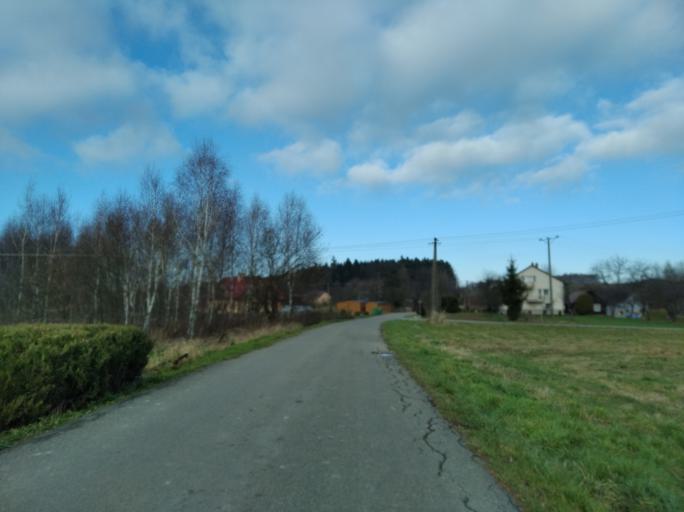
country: PL
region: Subcarpathian Voivodeship
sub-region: Powiat strzyzowski
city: Babica
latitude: 49.9050
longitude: 21.8503
